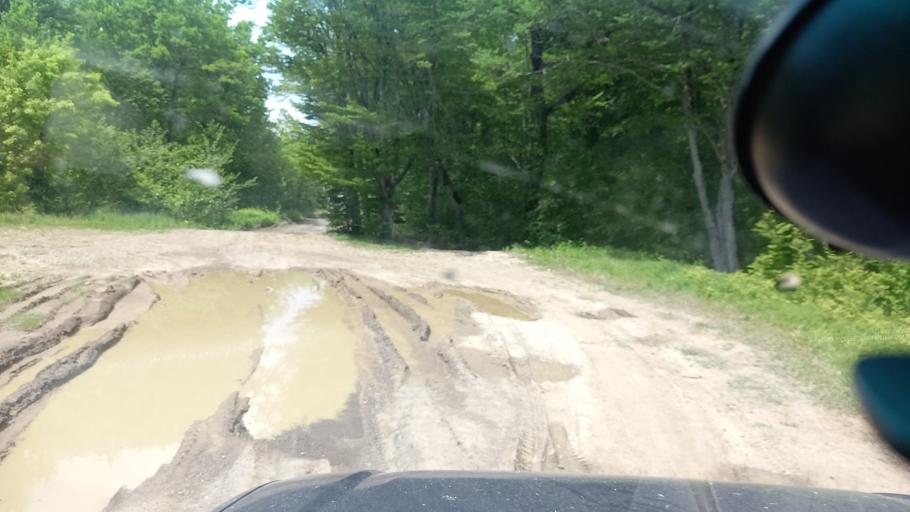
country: RU
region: Krasnodarskiy
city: Tuapse
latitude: 44.2641
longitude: 39.2736
